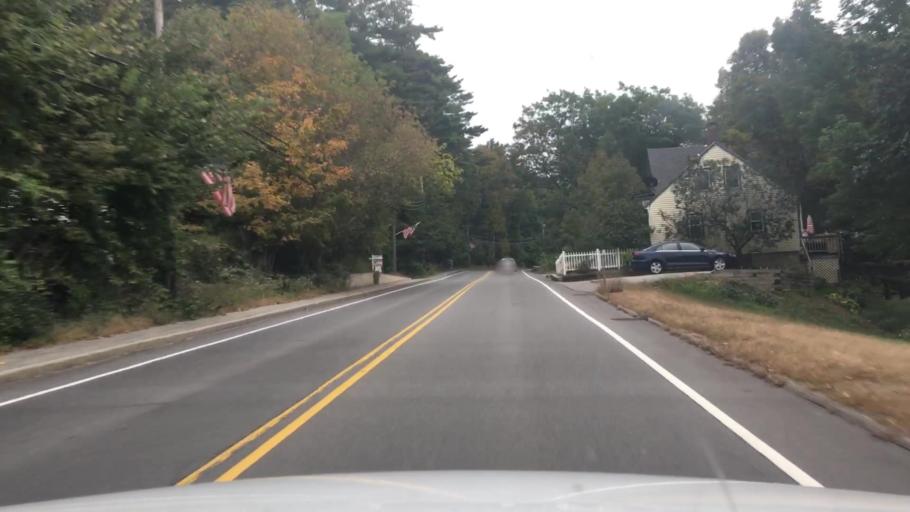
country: US
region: New Hampshire
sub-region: Strafford County
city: New Durham
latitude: 43.4639
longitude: -71.2285
